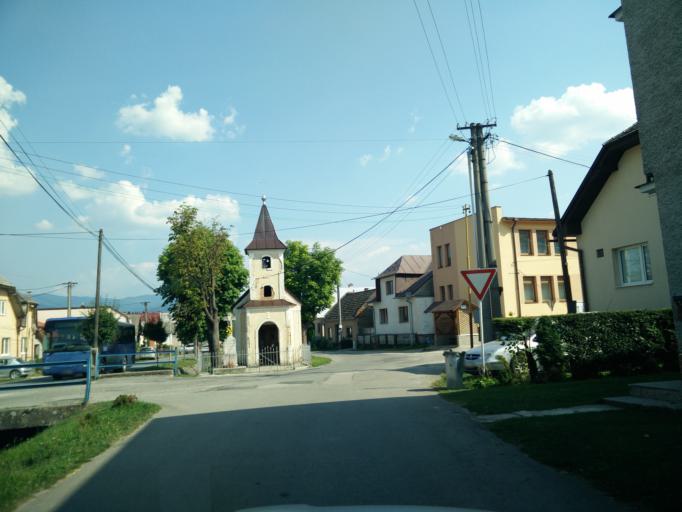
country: SK
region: Zilinsky
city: Rajec
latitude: 49.1110
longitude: 18.6357
